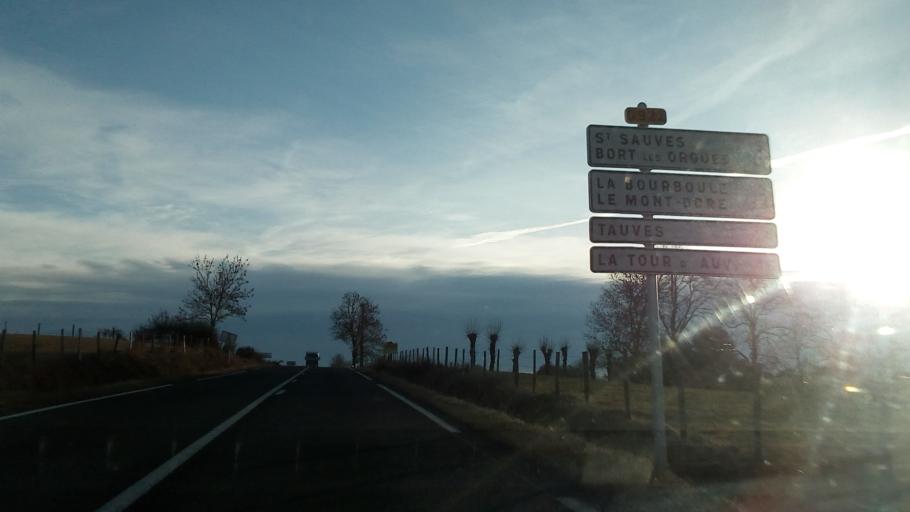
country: FR
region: Auvergne
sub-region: Departement du Puy-de-Dome
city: La Bourboule
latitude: 45.6401
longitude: 2.7237
